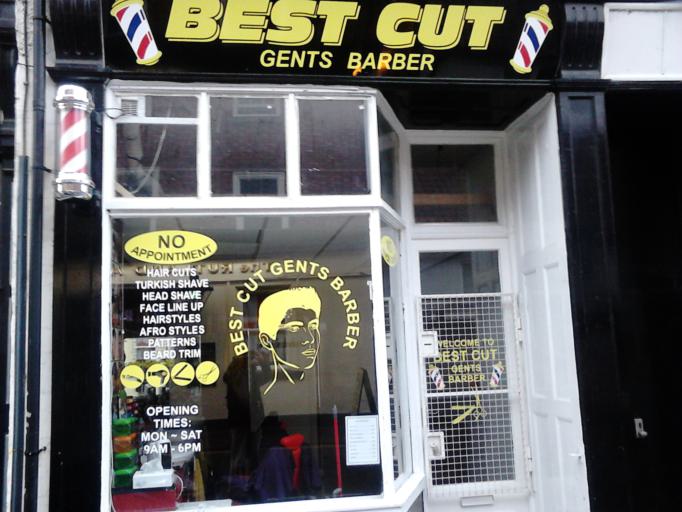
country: GB
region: England
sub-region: Nottinghamshire
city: Newark on Trent
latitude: 53.0757
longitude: -0.8070
